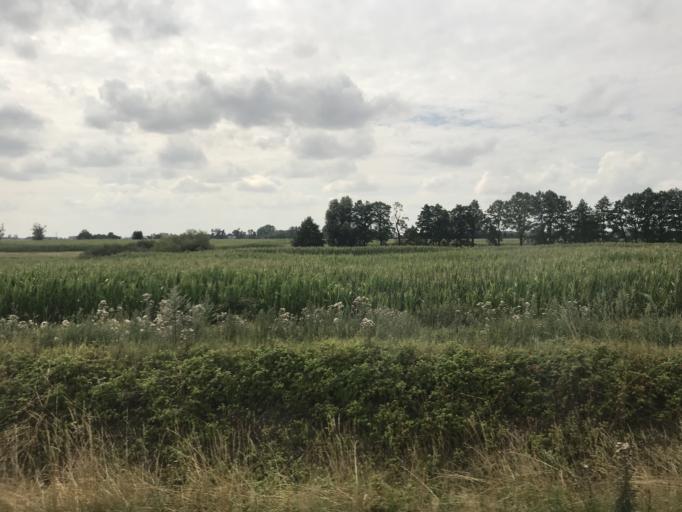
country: PL
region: Greater Poland Voivodeship
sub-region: Powiat gnieznienski
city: Niechanowo
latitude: 52.5336
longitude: 17.6668
